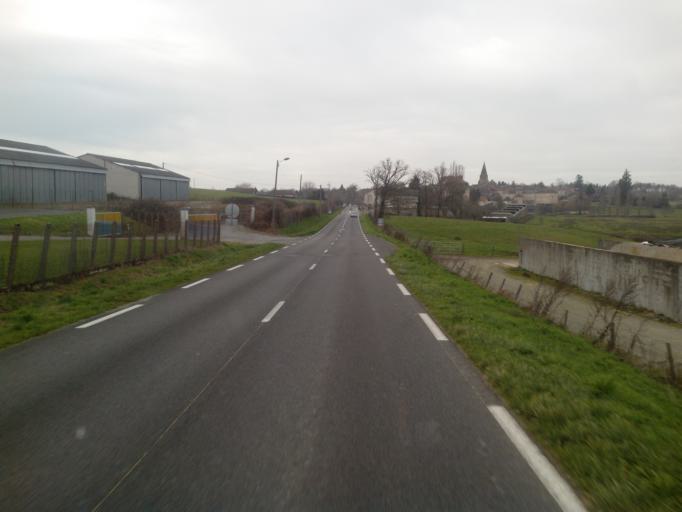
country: FR
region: Limousin
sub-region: Departement de la Haute-Vienne
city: Magnac-Laval
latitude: 46.2111
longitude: 1.1776
